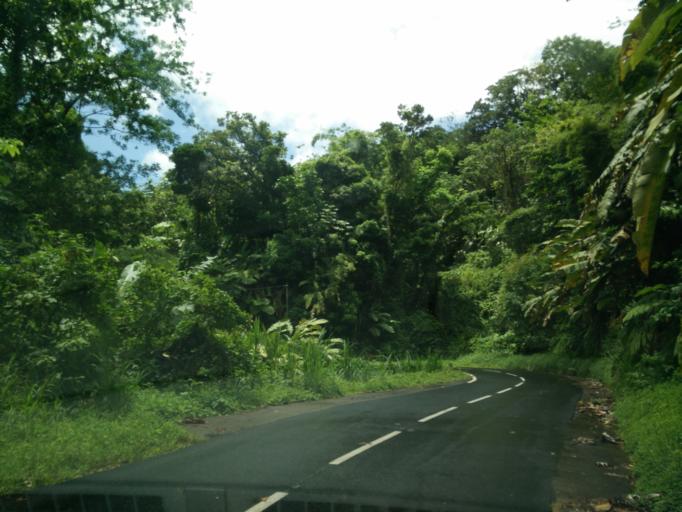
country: MQ
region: Martinique
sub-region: Martinique
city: Le Morne-Rouge
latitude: 14.7319
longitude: -61.1217
